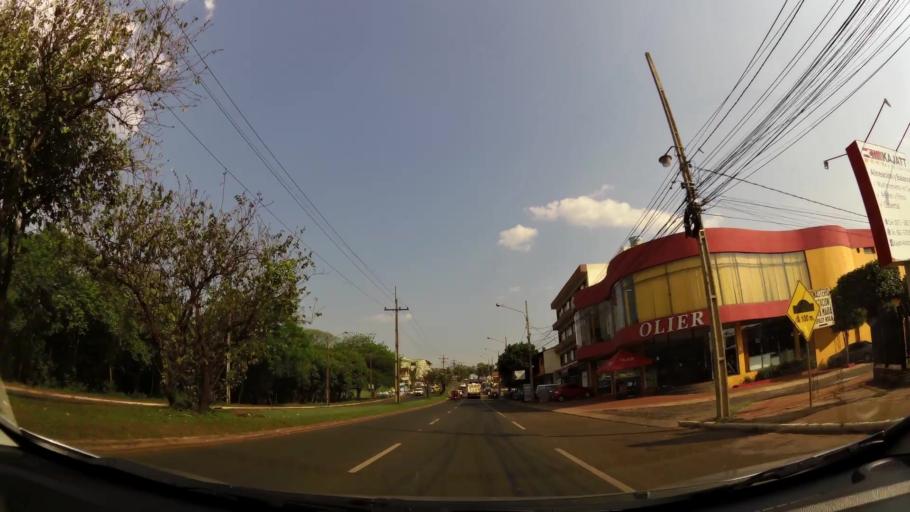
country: PY
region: Alto Parana
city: Presidente Franco
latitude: -25.5311
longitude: -54.6352
